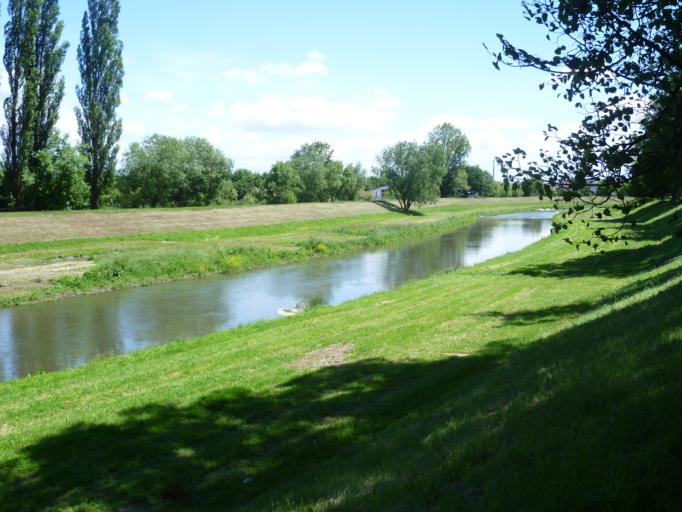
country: CZ
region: Moravskoslezsky
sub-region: Okres Opava
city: Opava
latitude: 49.9493
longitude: 17.8947
